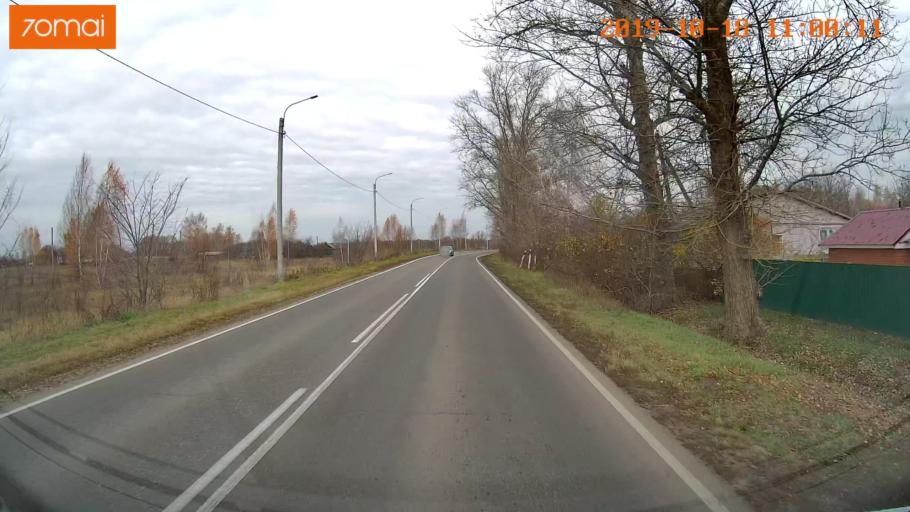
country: RU
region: Tula
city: Yepifan'
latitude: 53.8399
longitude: 38.5530
